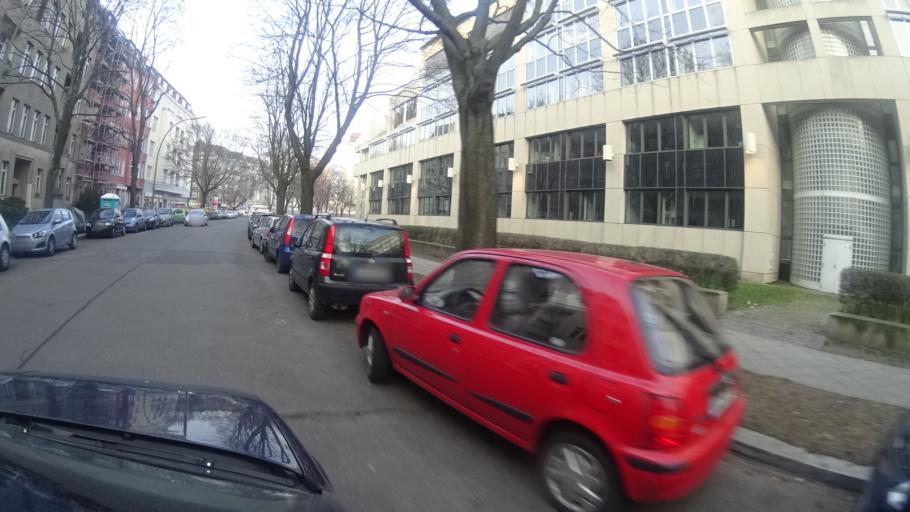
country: DE
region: Berlin
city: Tempelhof Bezirk
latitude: 52.4825
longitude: 13.3846
